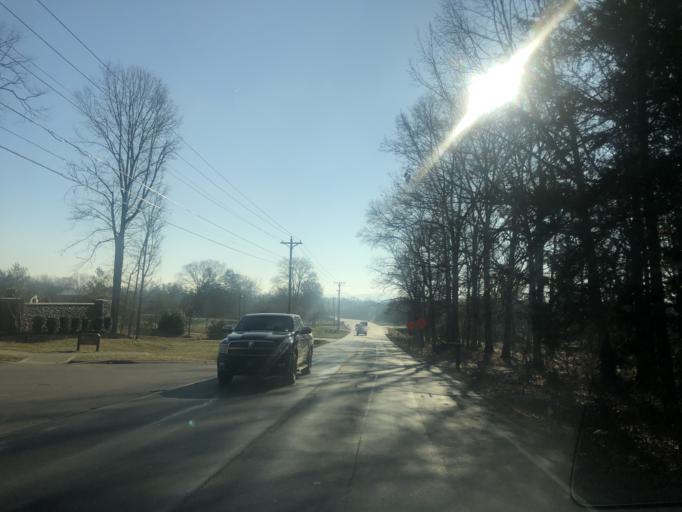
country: US
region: Tennessee
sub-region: Williamson County
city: Nolensville
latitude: 35.9652
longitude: -86.6938
